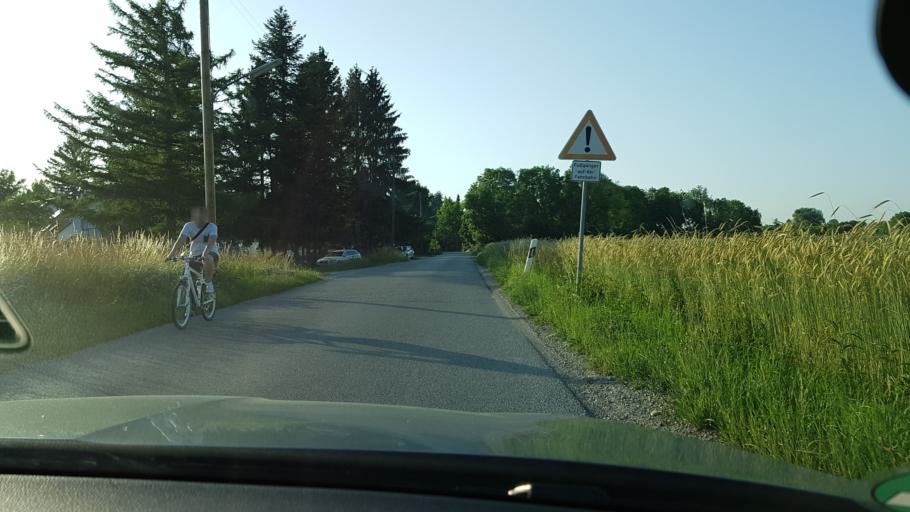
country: DE
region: Bavaria
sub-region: Upper Bavaria
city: Bogenhausen
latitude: 48.1543
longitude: 11.6563
